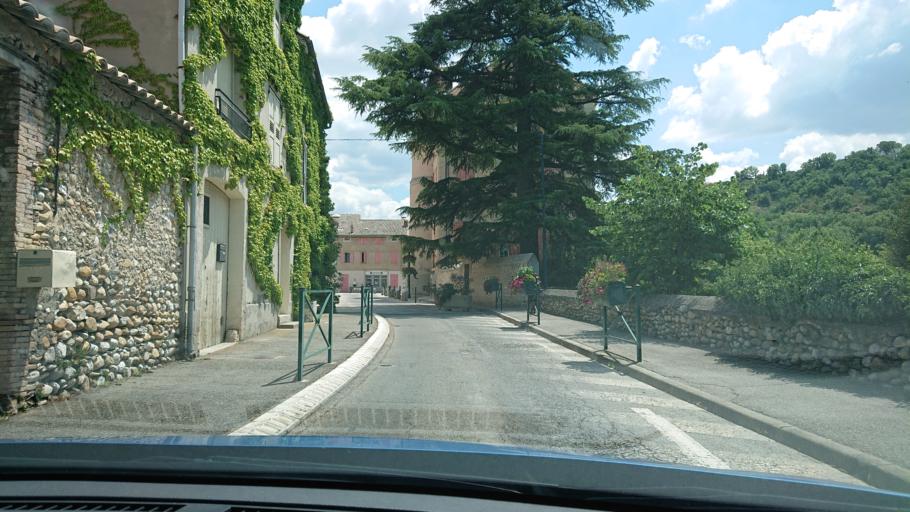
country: FR
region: Provence-Alpes-Cote d'Azur
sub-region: Departement des Alpes-de-Haute-Provence
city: Malijai
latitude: 44.0453
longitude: 6.0289
